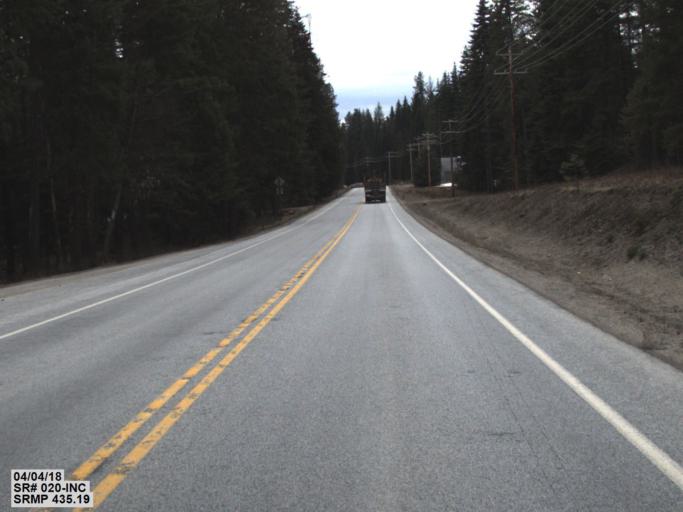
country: US
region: Washington
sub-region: Pend Oreille County
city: Newport
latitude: 48.2038
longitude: -117.0641
